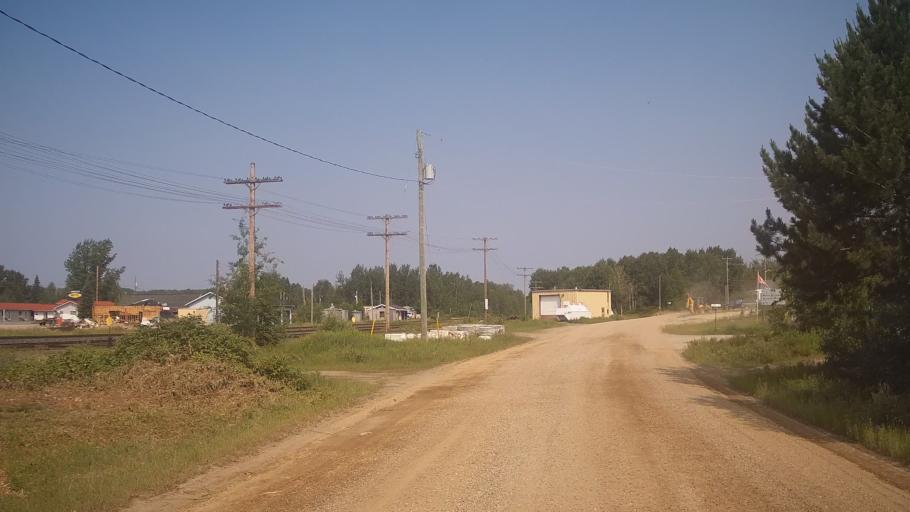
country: CA
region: Ontario
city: Timmins
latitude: 47.6758
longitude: -81.7228
